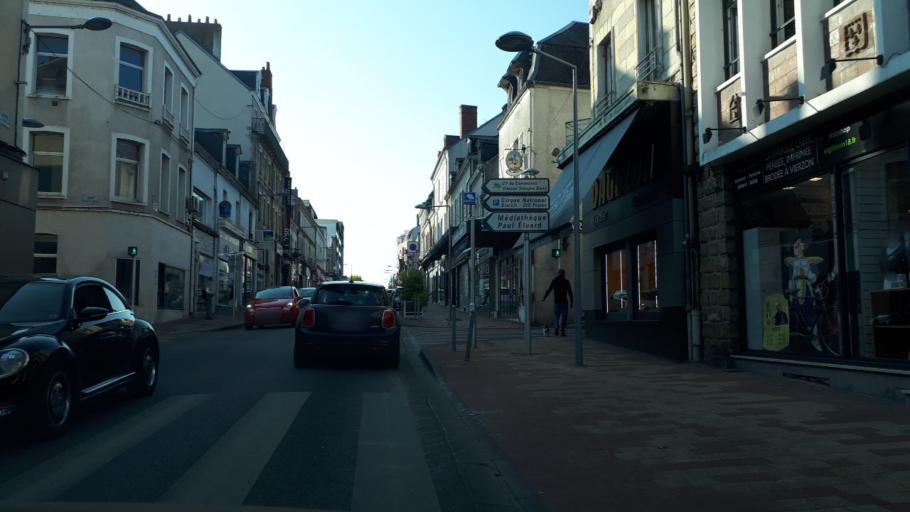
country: FR
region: Centre
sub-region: Departement du Cher
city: Vierzon
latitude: 47.2229
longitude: 2.0662
